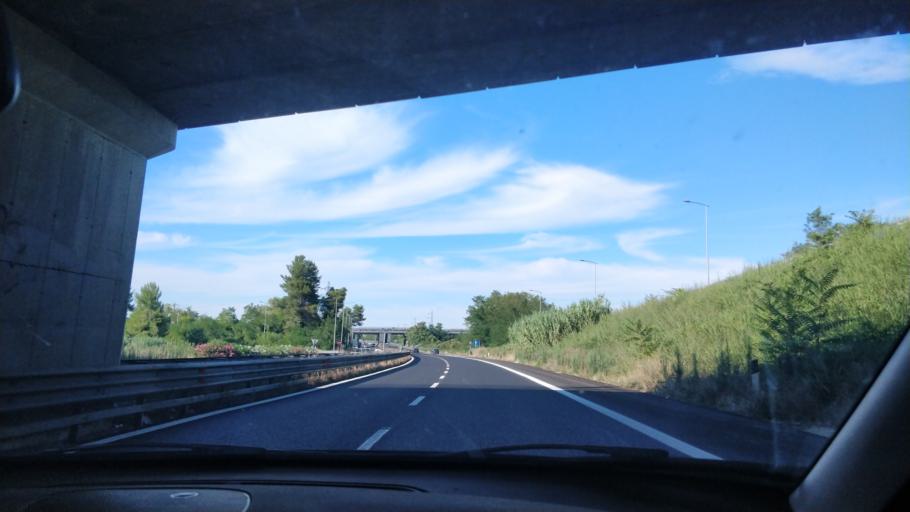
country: IT
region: Abruzzo
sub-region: Provincia di Chieti
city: Chieti
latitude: 42.3959
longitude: 14.1609
